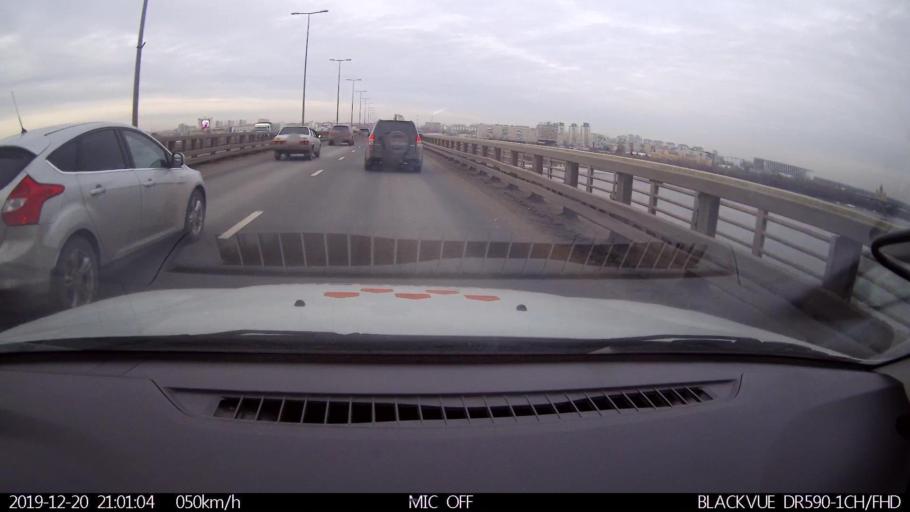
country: RU
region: Nizjnij Novgorod
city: Nizhniy Novgorod
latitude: 56.3175
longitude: 43.9678
